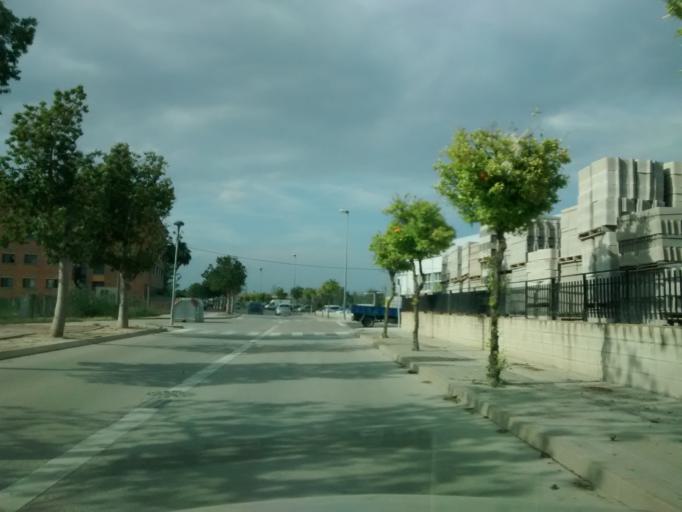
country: ES
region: Catalonia
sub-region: Provincia de Tarragona
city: Deltebre
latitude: 40.7205
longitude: 0.7212
